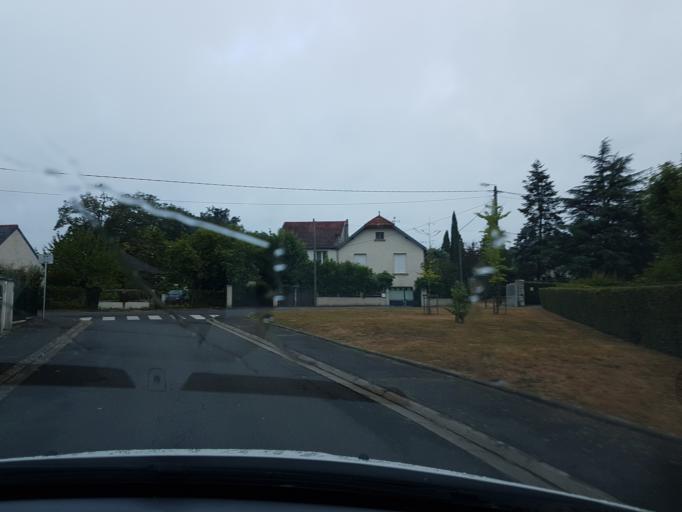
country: FR
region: Centre
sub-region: Departement d'Indre-et-Loire
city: Saint-Avertin
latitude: 47.3618
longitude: 0.7385
